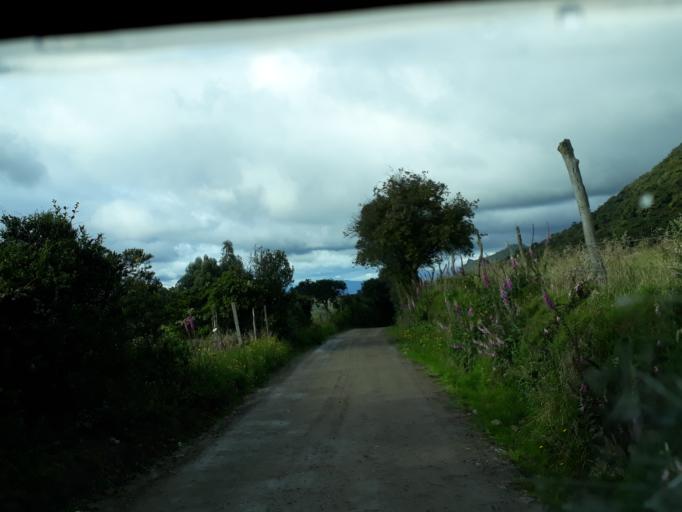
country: CO
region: Cundinamarca
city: Sutatausa
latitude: 5.1905
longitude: -73.8946
